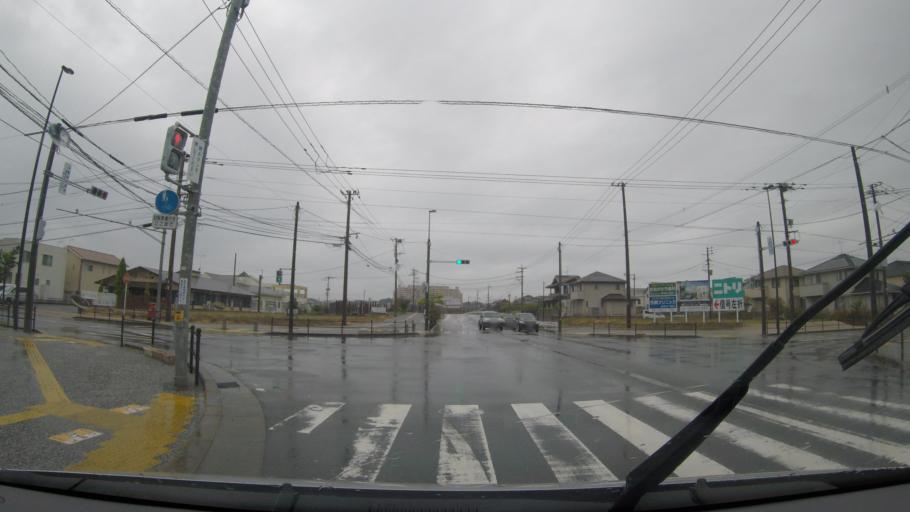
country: JP
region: Fukuoka
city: Koga
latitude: 33.7221
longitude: 130.4630
